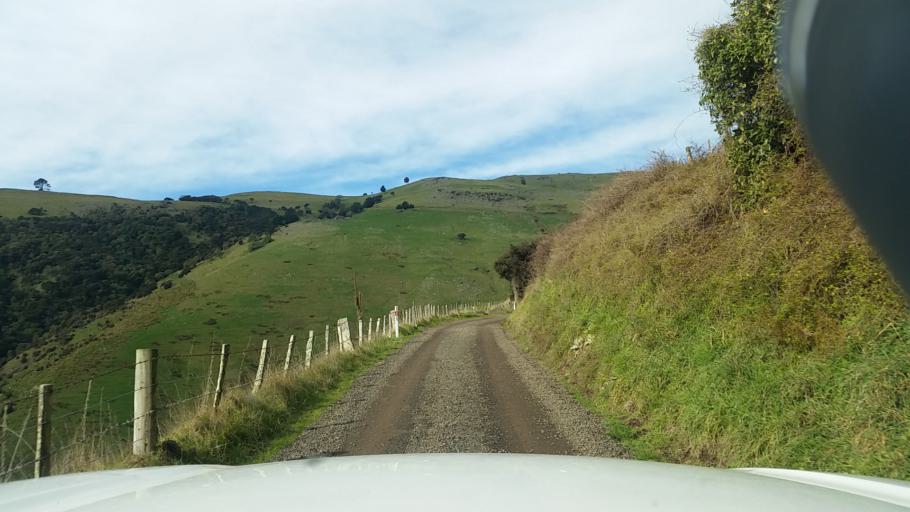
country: NZ
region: Canterbury
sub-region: Christchurch City
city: Christchurch
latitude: -43.6756
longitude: 172.8337
